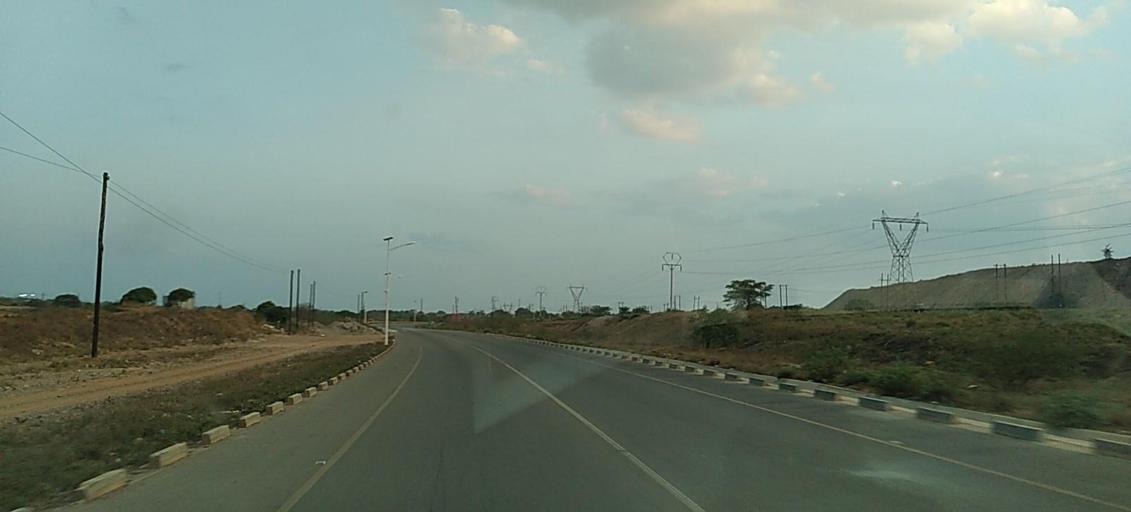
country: ZM
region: Copperbelt
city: Chingola
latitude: -12.5304
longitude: 27.8362
